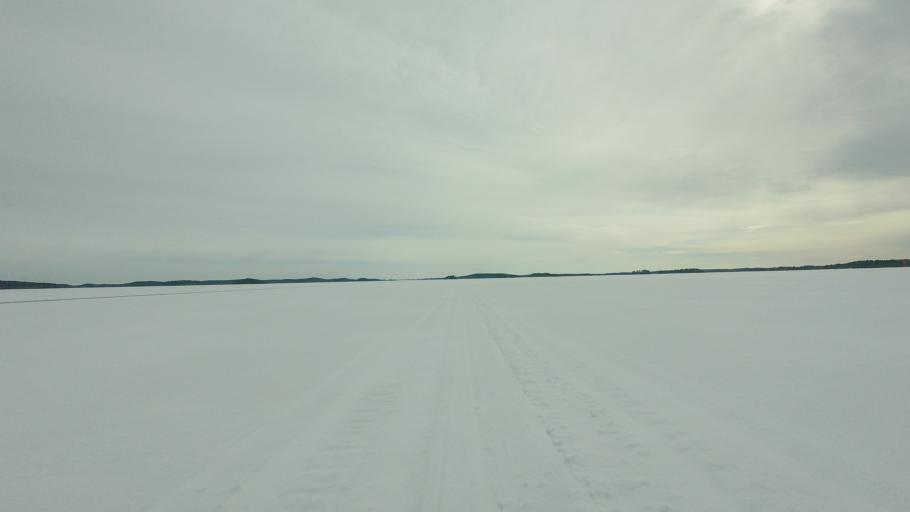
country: FI
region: Southern Savonia
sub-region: Savonlinna
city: Rantasalmi
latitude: 62.1101
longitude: 28.3926
